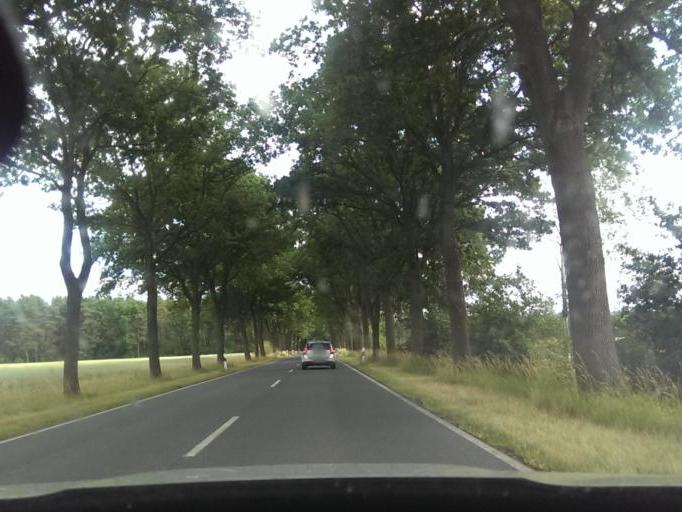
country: DE
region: Lower Saxony
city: Essel
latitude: 52.6576
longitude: 9.6697
